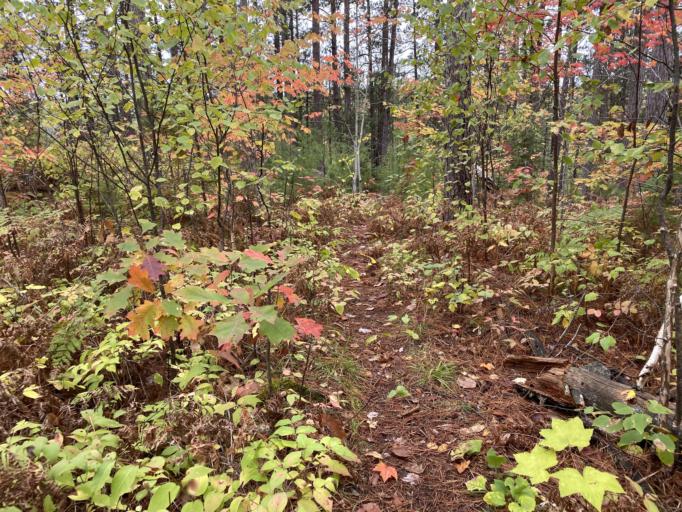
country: US
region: Michigan
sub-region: Marquette County
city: West Ishpeming
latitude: 46.5395
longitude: -87.9987
